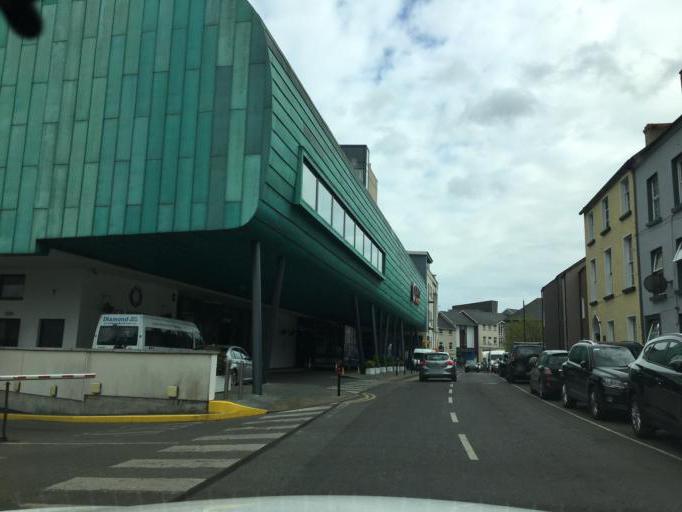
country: IE
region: Leinster
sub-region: Loch Garman
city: Loch Garman
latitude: 52.3405
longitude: -6.4647
